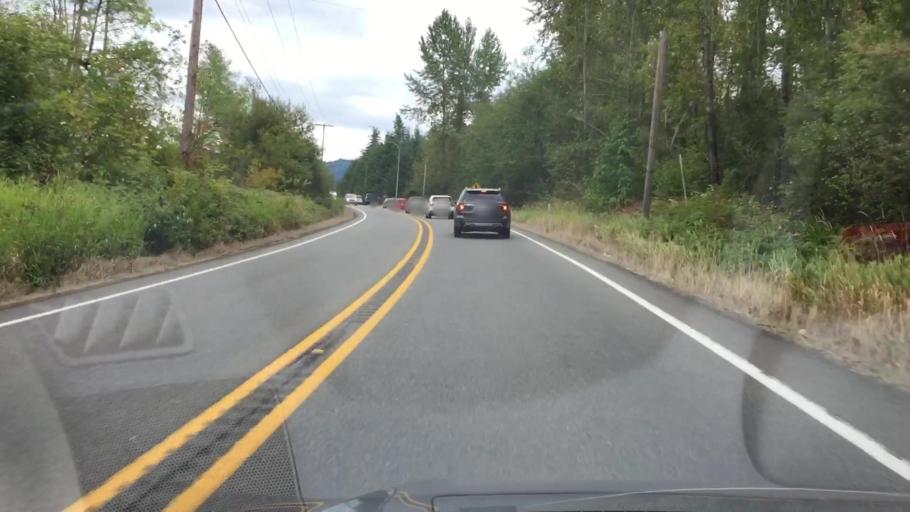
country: US
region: Washington
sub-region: Pierce County
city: Eatonville
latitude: 46.9518
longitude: -122.2963
